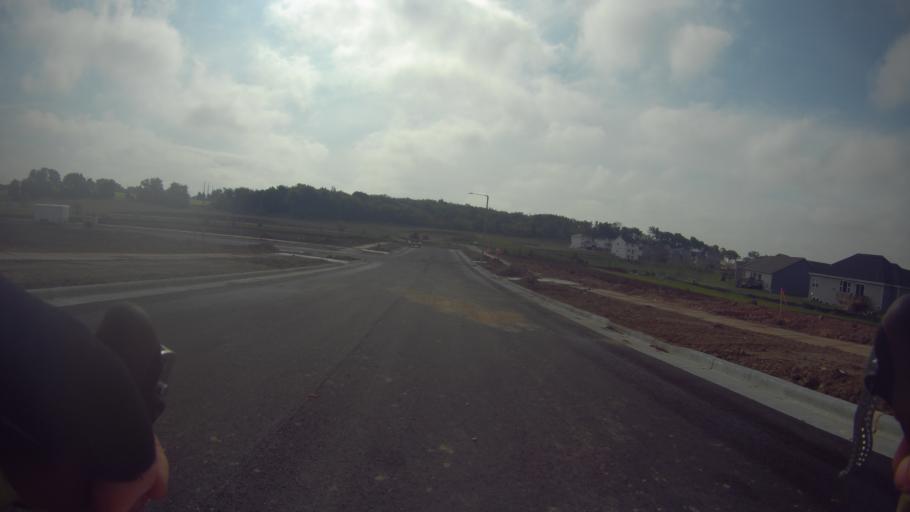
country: US
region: Wisconsin
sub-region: Dane County
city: McFarland
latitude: 43.0240
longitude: -89.2749
